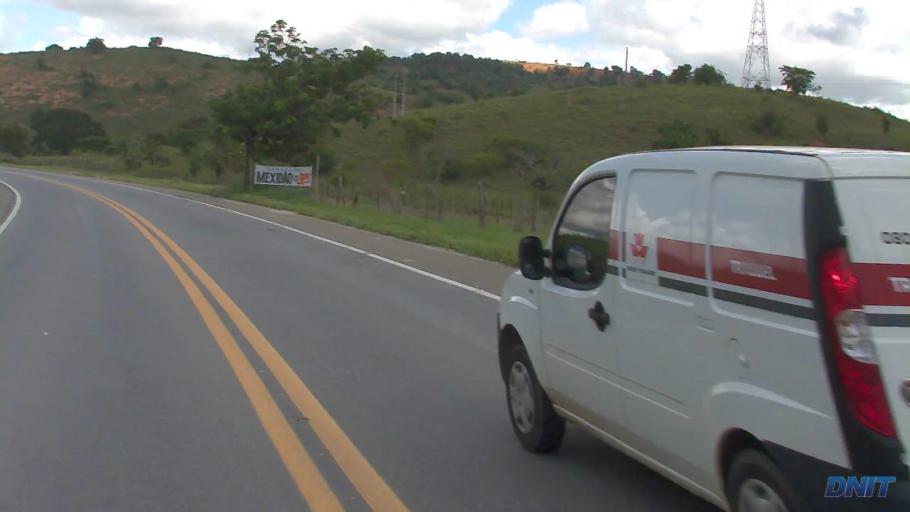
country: BR
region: Minas Gerais
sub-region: Governador Valadares
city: Governador Valadares
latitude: -18.9775
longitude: -42.0989
